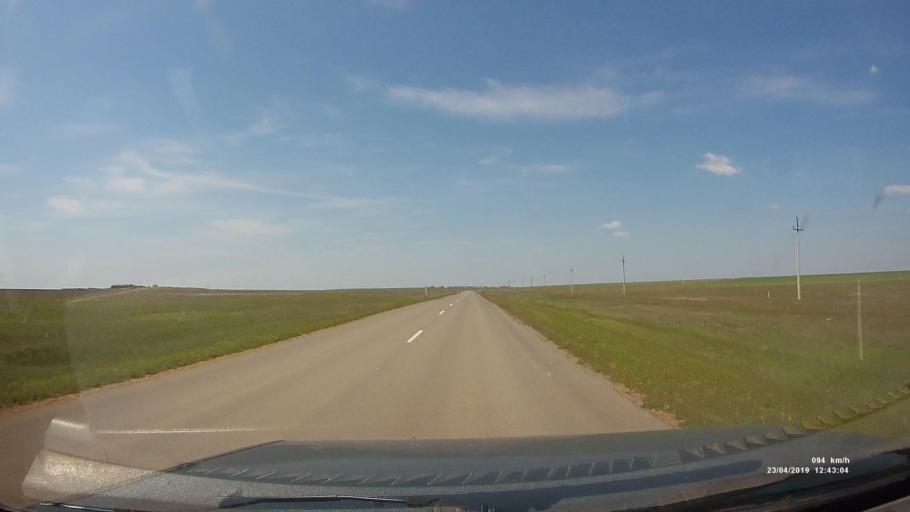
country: RU
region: Kalmykiya
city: Yashalta
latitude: 46.4610
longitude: 42.6557
